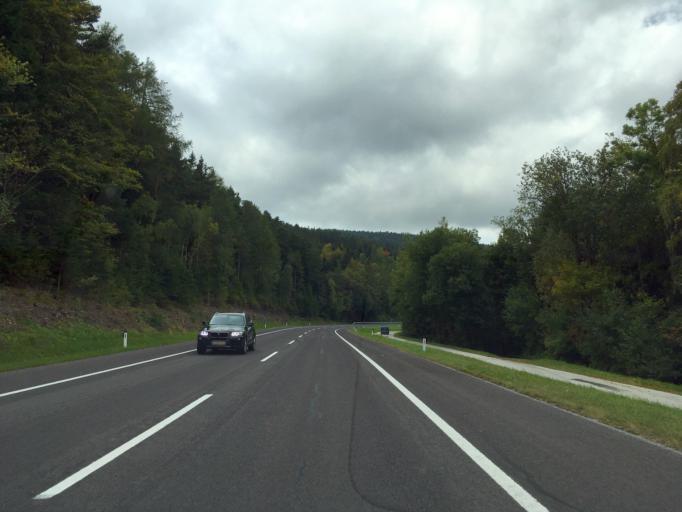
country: AT
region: Lower Austria
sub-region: Politischer Bezirk Neunkirchen
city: Monichkirchen
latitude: 47.5030
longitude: 16.0322
